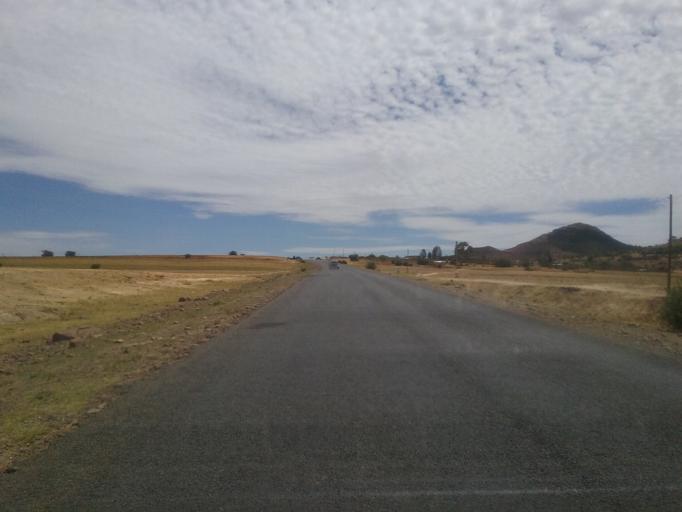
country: LS
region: Mafeteng
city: Mafeteng
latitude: -29.8643
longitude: 27.2362
